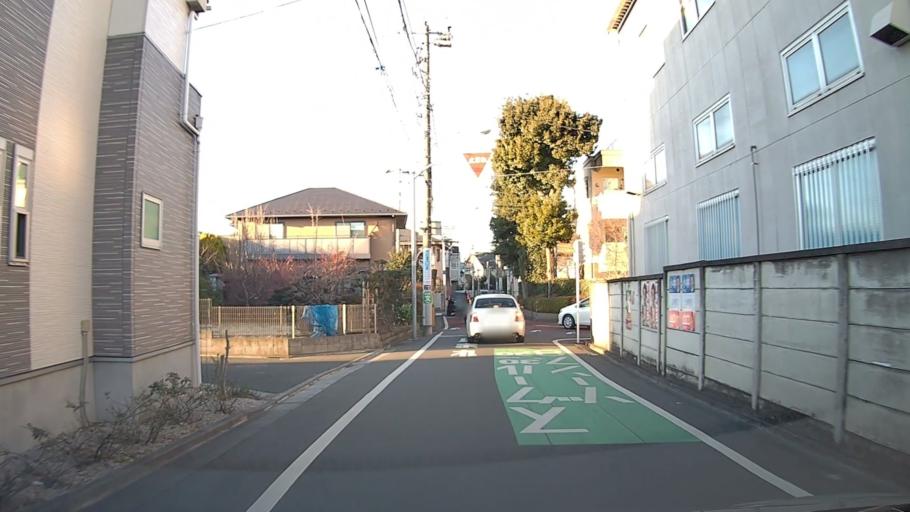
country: JP
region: Tokyo
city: Musashino
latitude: 35.7353
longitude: 139.6065
